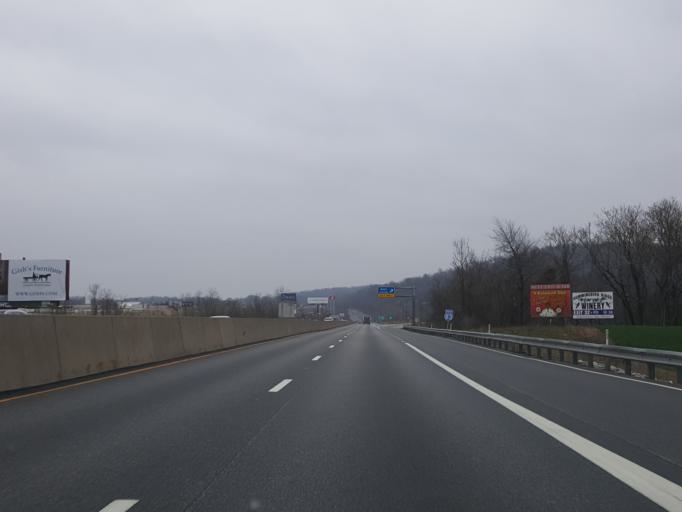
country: US
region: Pennsylvania
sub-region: York County
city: Valley Green
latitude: 40.1598
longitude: -76.8249
